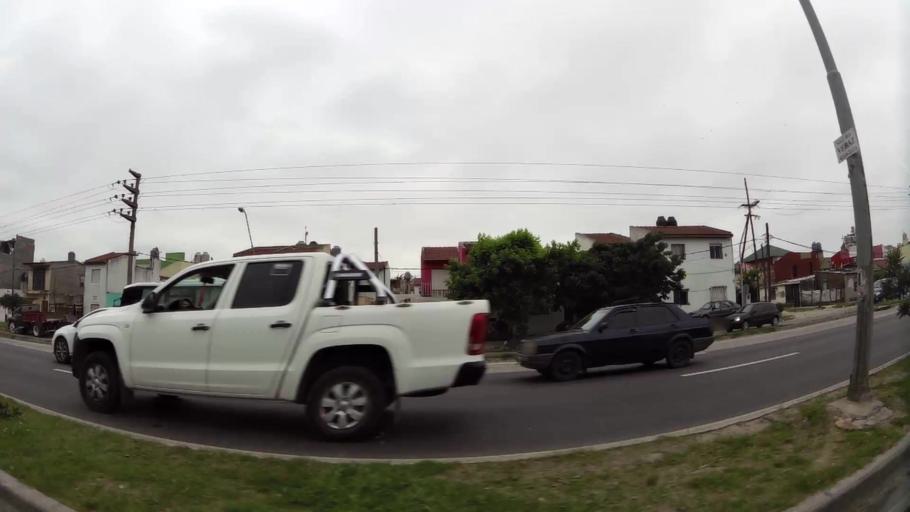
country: AR
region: Buenos Aires
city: San Justo
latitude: -34.6963
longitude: -58.5463
